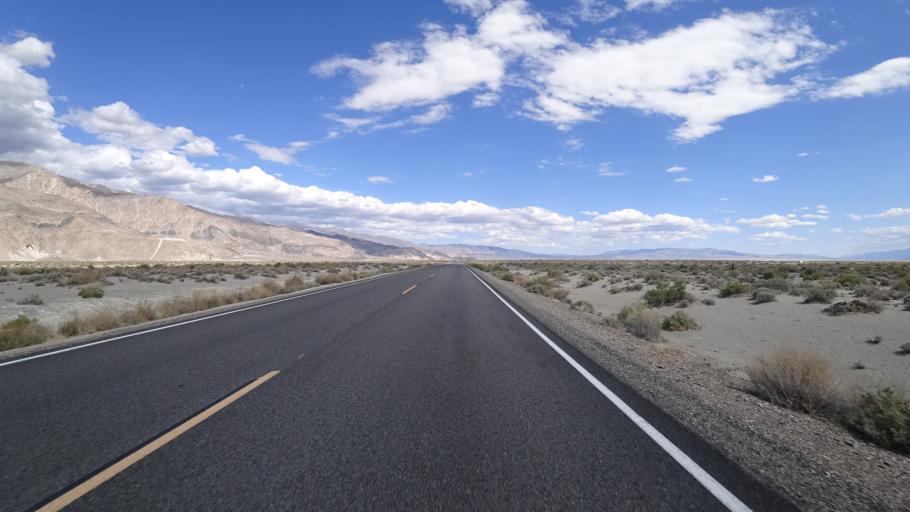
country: US
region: California
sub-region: Inyo County
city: Lone Pine
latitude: 36.5704
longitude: -117.9878
